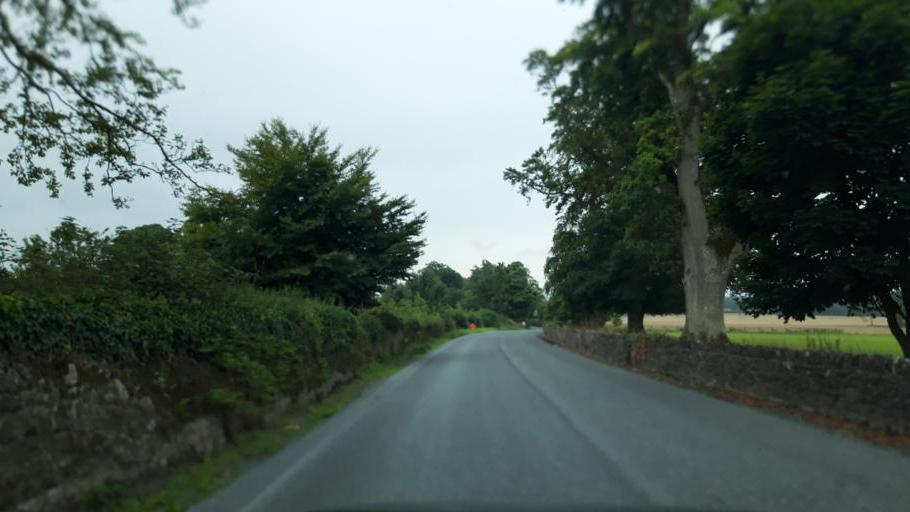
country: IE
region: Munster
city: Fethard
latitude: 52.4365
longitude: -7.6993
